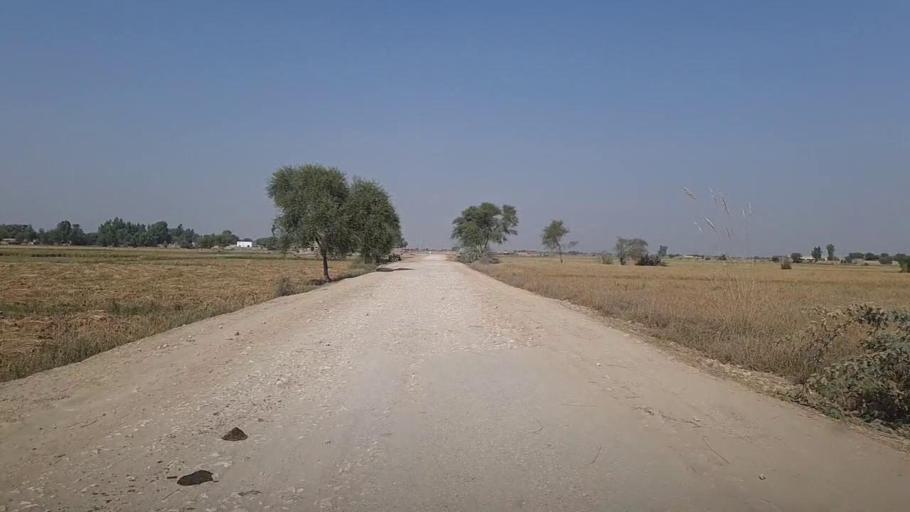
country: PK
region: Sindh
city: Kandhkot
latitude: 28.3925
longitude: 69.3264
